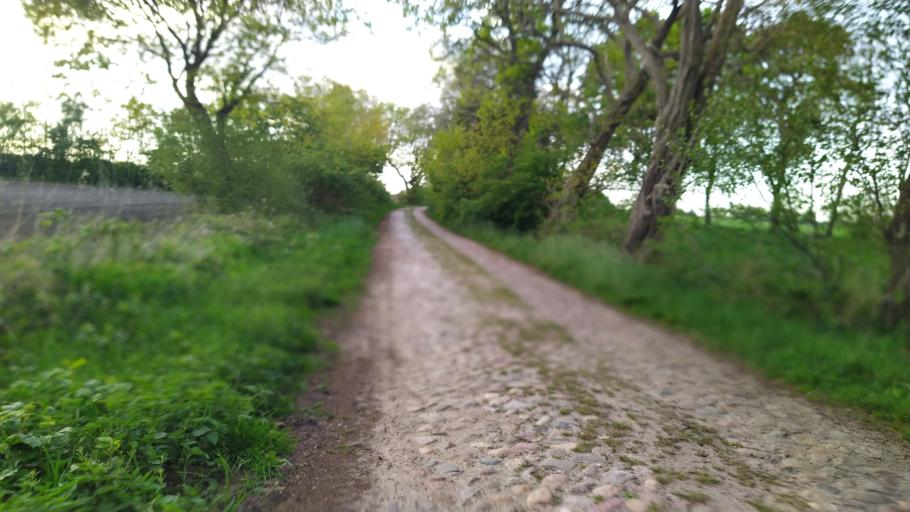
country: DE
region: Lower Saxony
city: Farven
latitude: 53.4318
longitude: 9.3326
